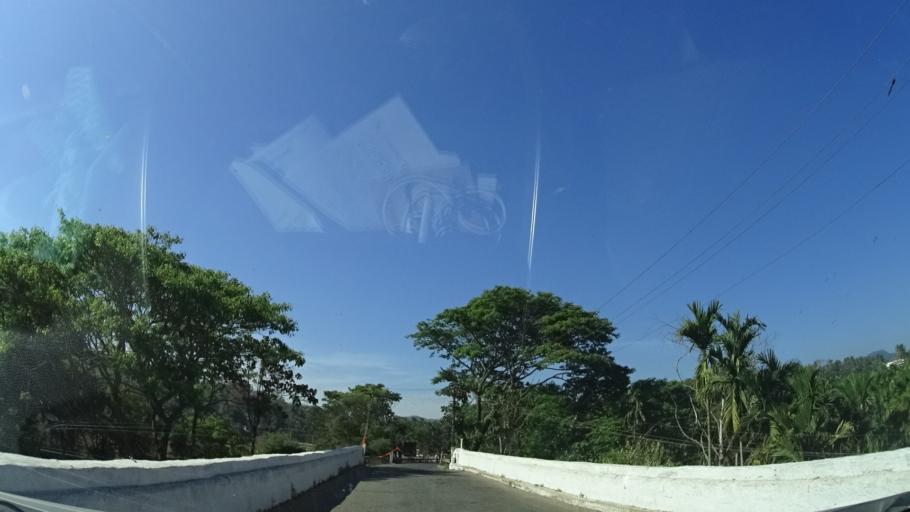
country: IN
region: Karnataka
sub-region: Chikmagalur
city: Koppa
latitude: 13.3512
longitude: 75.4704
